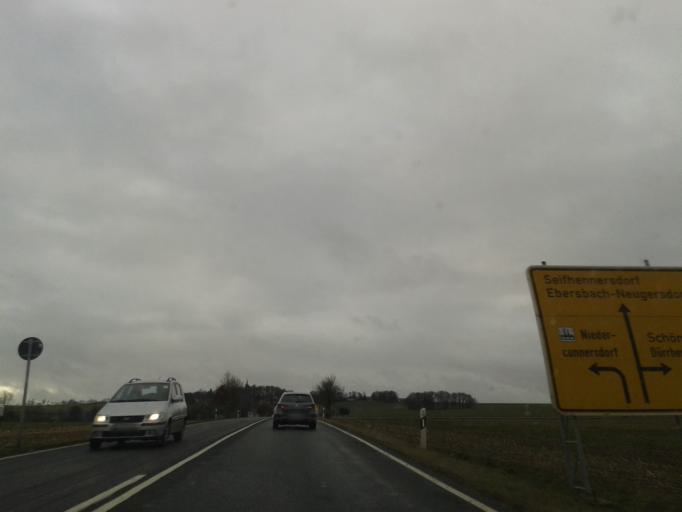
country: DE
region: Saxony
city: Durrhennersdorf
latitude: 51.0457
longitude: 14.6351
